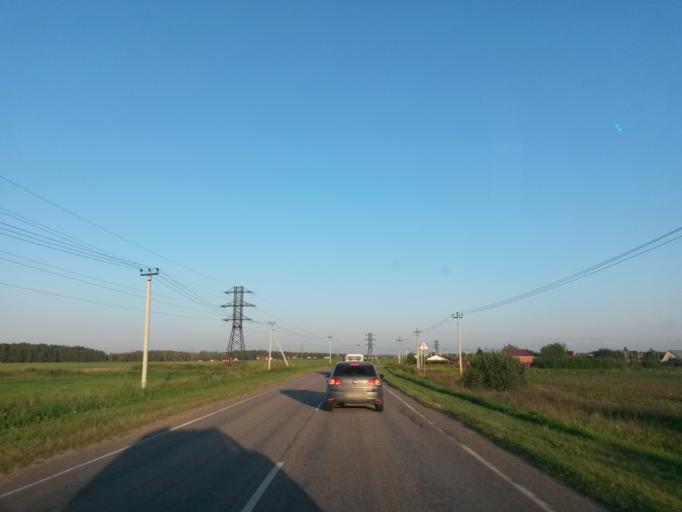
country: RU
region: Moskovskaya
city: Barybino
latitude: 55.2491
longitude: 37.7921
